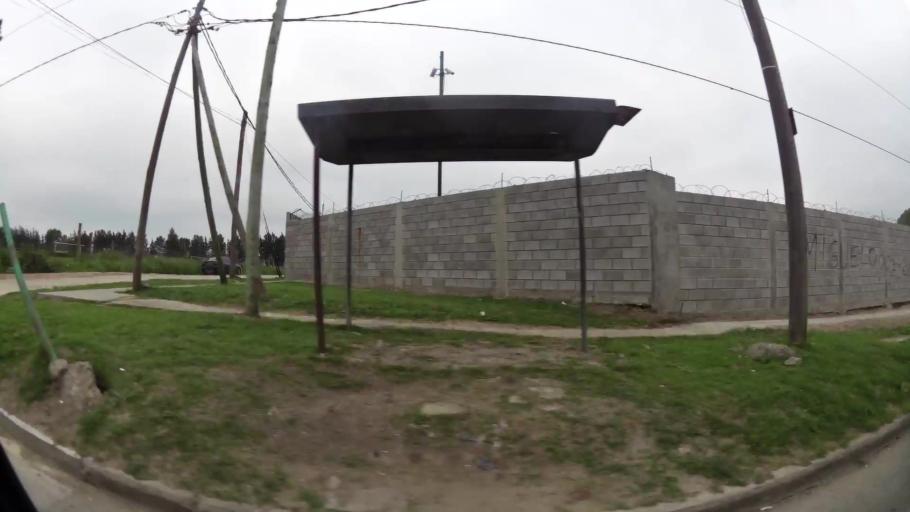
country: AR
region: Buenos Aires
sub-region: Partido de La Plata
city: La Plata
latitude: -34.9381
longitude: -58.0017
